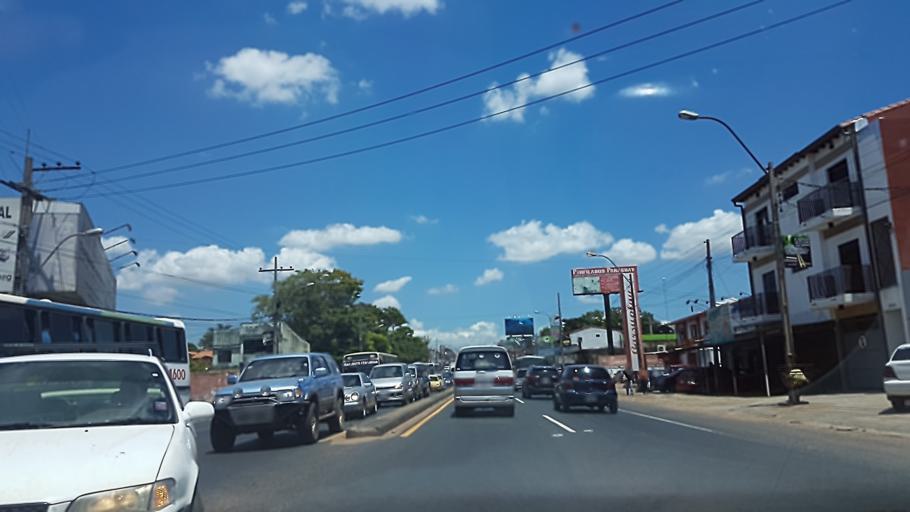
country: PY
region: Central
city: San Lorenzo
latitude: -25.3431
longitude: -57.4907
